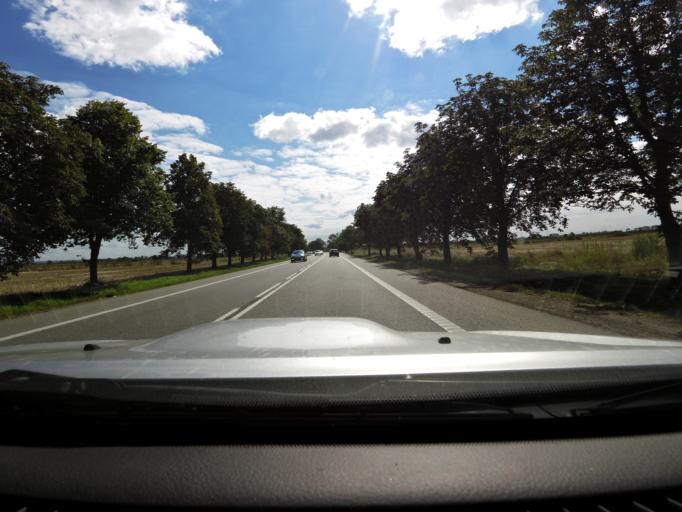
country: PL
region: Pomeranian Voivodeship
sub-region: Powiat nowodworski
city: Nowy Dwor Gdanski
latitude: 54.1810
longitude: 19.2258
